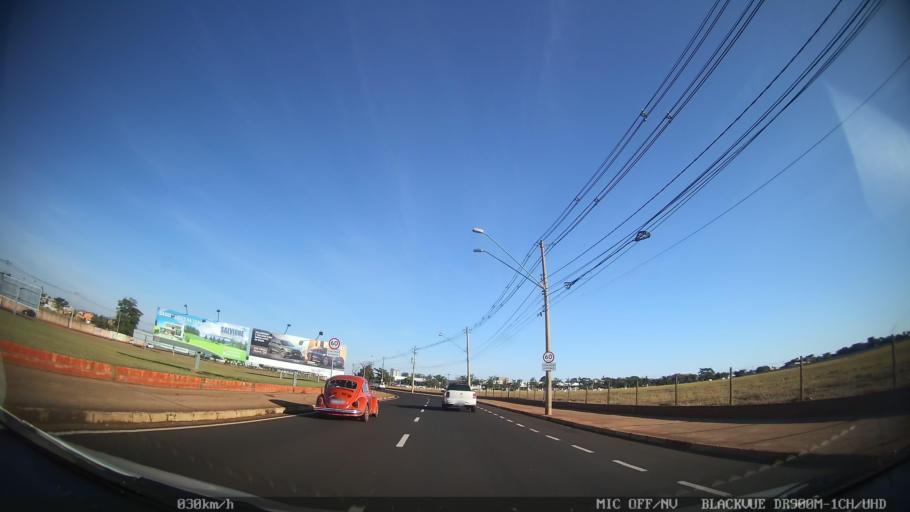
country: BR
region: Sao Paulo
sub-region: Sao Jose Do Rio Preto
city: Sao Jose do Rio Preto
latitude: -20.8517
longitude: -49.4134
